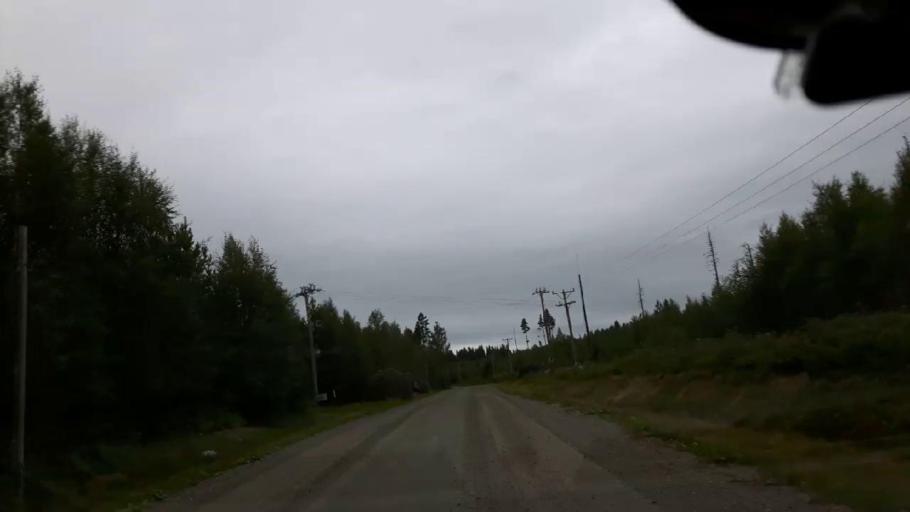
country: SE
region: Vaesternorrland
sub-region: Ange Kommun
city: Fransta
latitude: 62.7908
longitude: 16.0411
